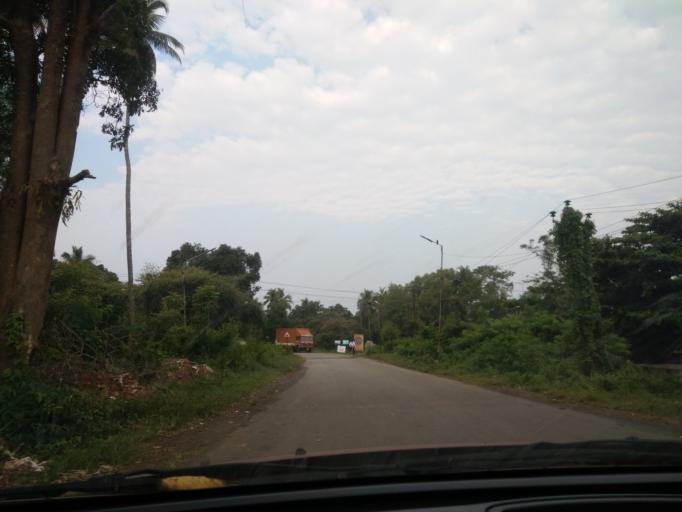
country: IN
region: Goa
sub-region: South Goa
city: Varca
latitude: 15.2200
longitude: 73.9574
